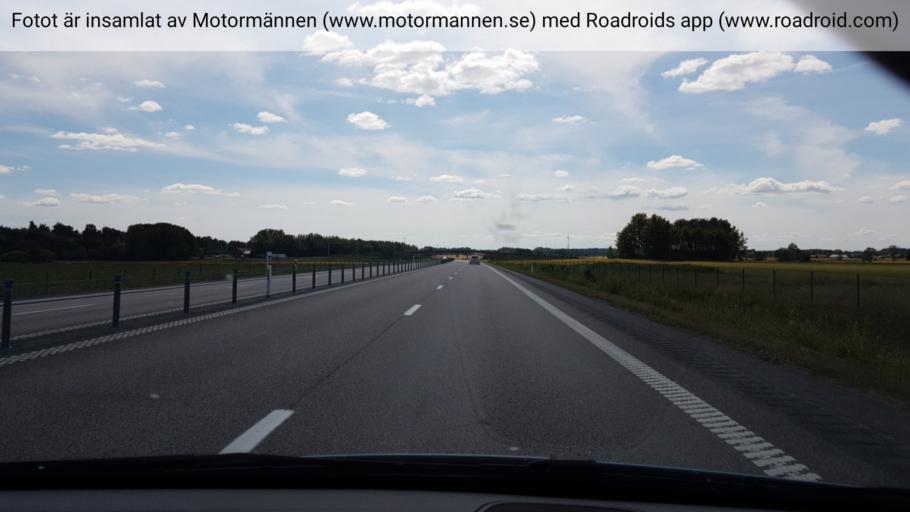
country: SE
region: Vaestra Goetaland
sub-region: Gotene Kommun
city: Goetene
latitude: 58.5254
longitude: 13.5142
